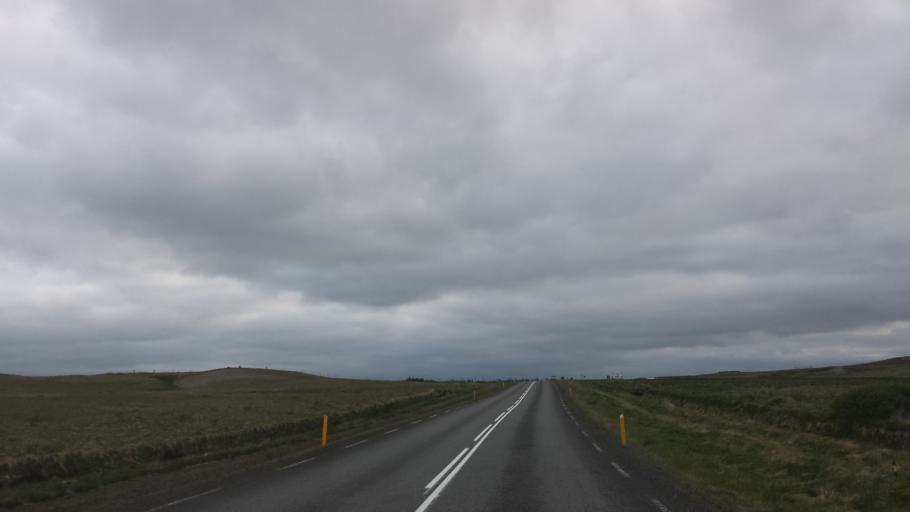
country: IS
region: South
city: Selfoss
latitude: 64.1243
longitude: -20.5970
